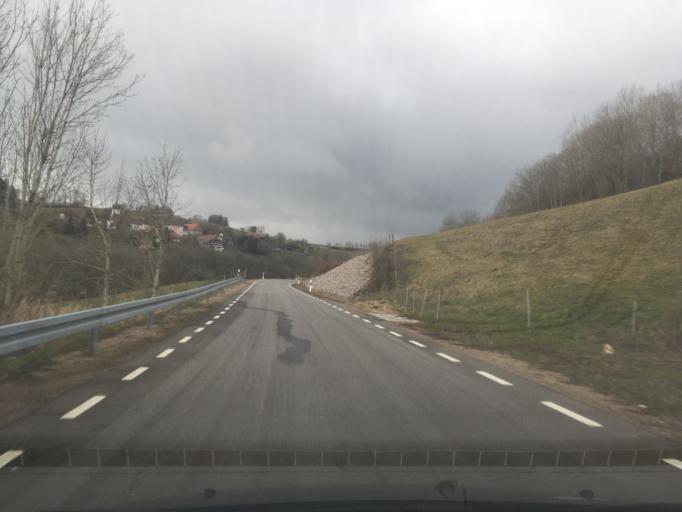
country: DE
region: Baden-Wuerttemberg
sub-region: Freiburg Region
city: Dogern
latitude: 47.6599
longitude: 8.1797
